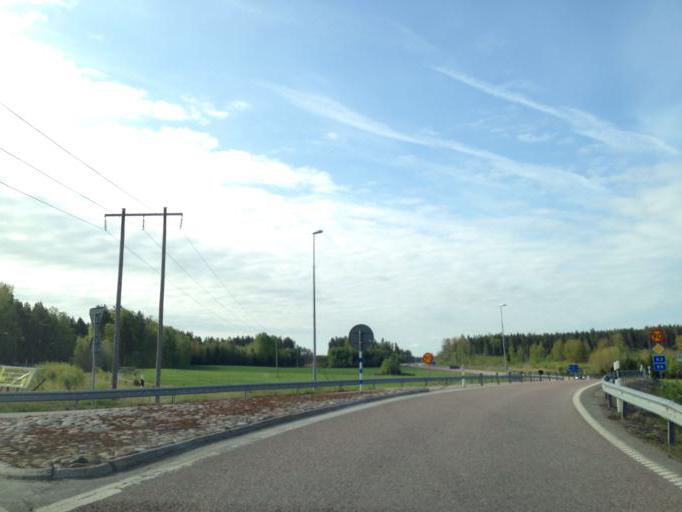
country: SE
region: Soedermanland
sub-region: Flens Kommun
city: Malmkoping
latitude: 59.1472
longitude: 16.7125
